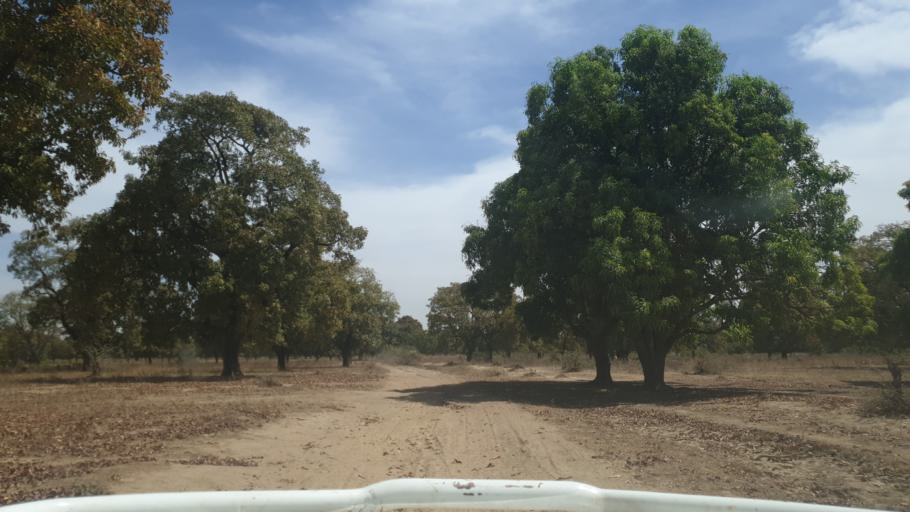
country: ML
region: Sikasso
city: Yorosso
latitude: 12.2918
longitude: -4.6658
